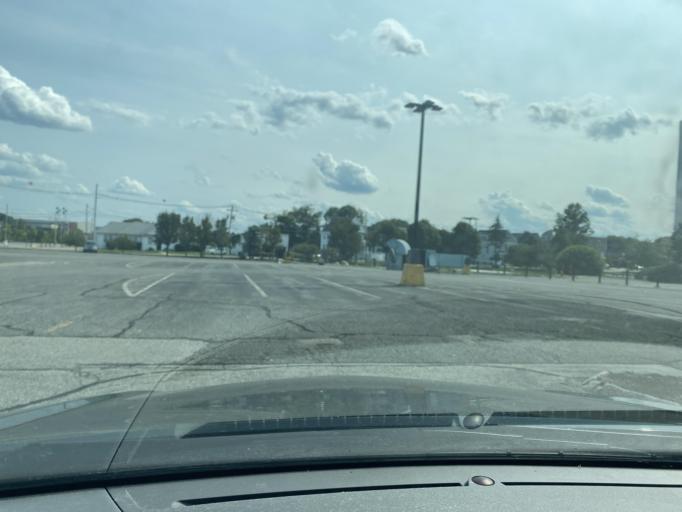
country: US
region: Massachusetts
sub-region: Norfolk County
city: Norwood
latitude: 42.1888
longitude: -71.2009
